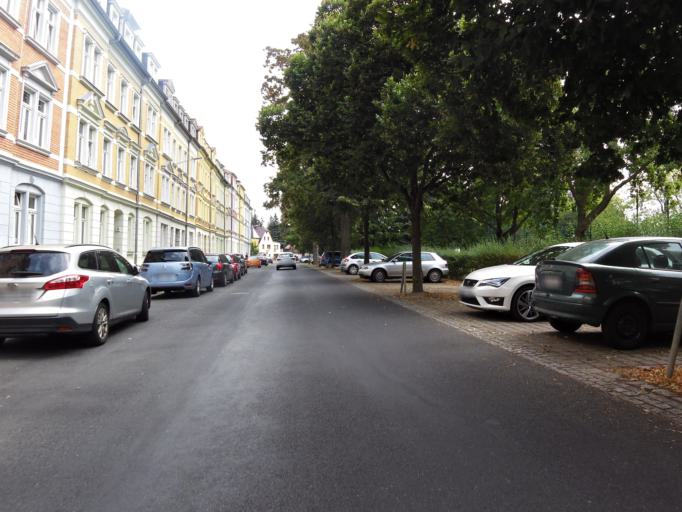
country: DE
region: Saxony
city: Dobeln
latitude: 51.1225
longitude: 13.1271
